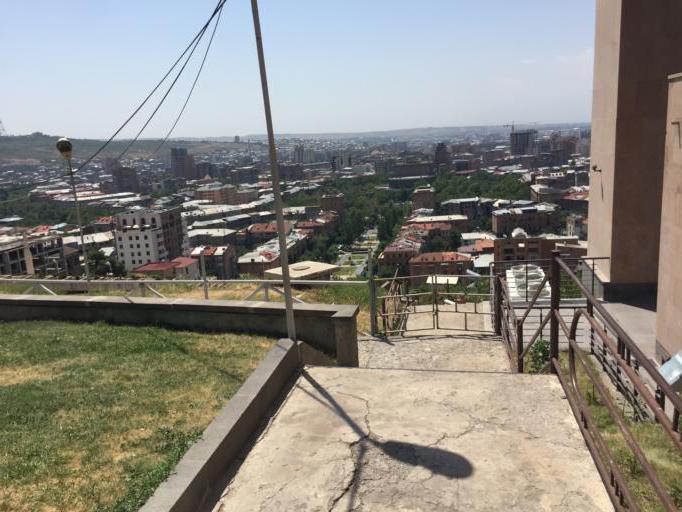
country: AM
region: Yerevan
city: Yerevan
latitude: 40.1930
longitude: 44.5150
